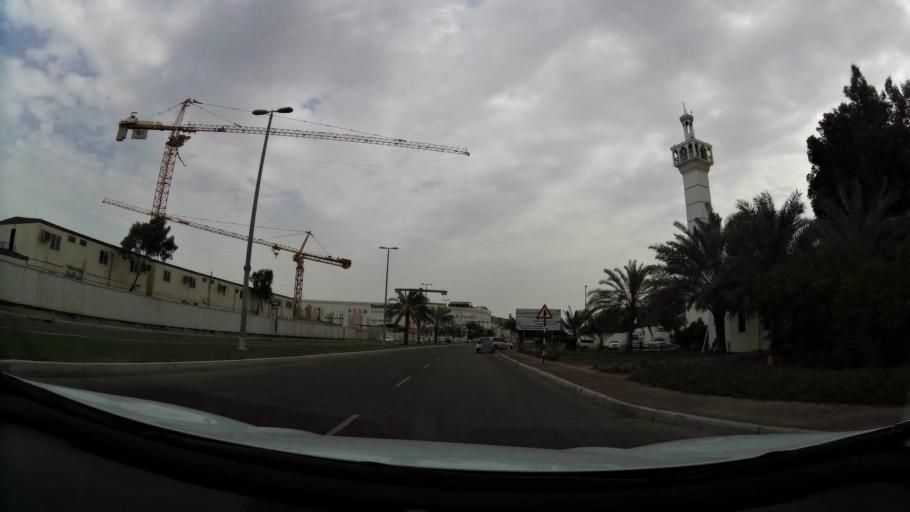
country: AE
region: Abu Dhabi
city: Abu Dhabi
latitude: 24.4233
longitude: 54.4488
